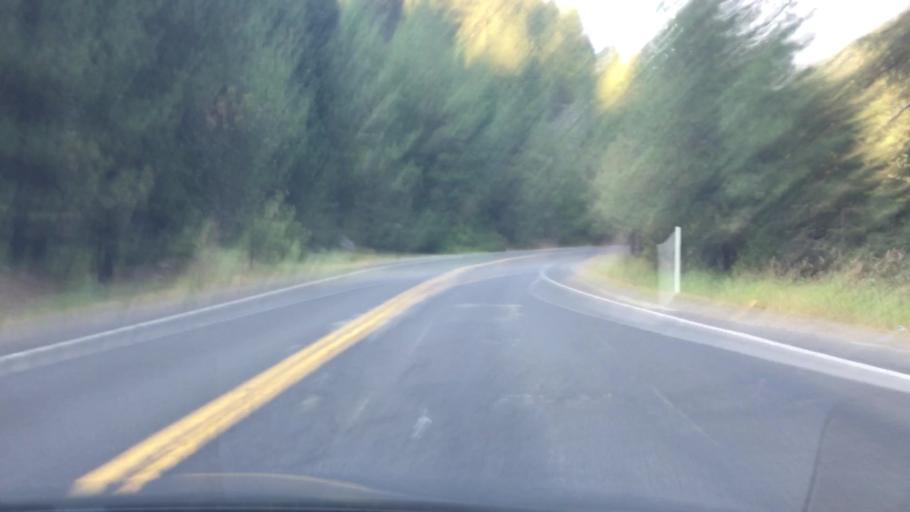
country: US
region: Idaho
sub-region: Valley County
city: Cascade
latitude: 44.2537
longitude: -116.0859
